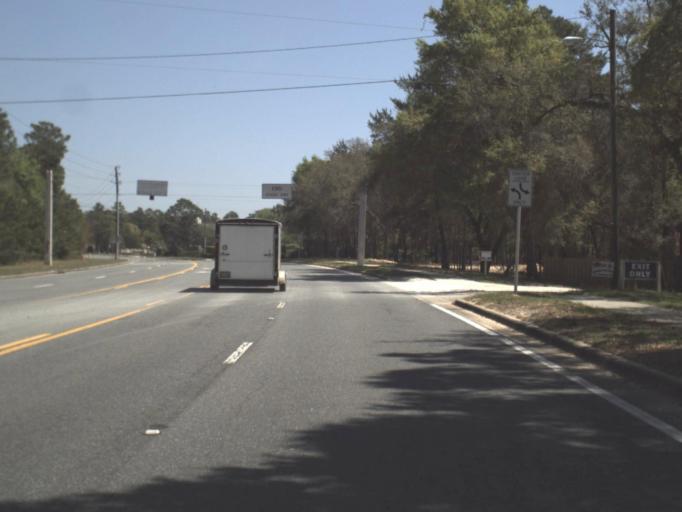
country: US
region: Florida
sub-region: Okaloosa County
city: Niceville
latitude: 30.5291
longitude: -86.4620
